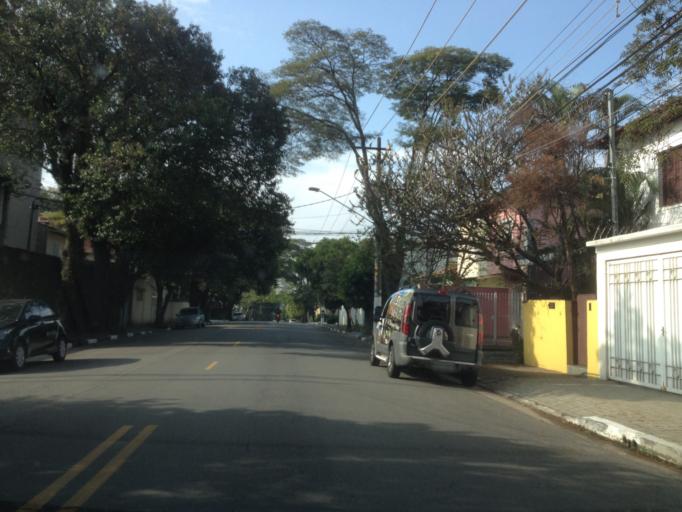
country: BR
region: Sao Paulo
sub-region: Sao Paulo
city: Sao Paulo
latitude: -23.6202
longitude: -46.6687
